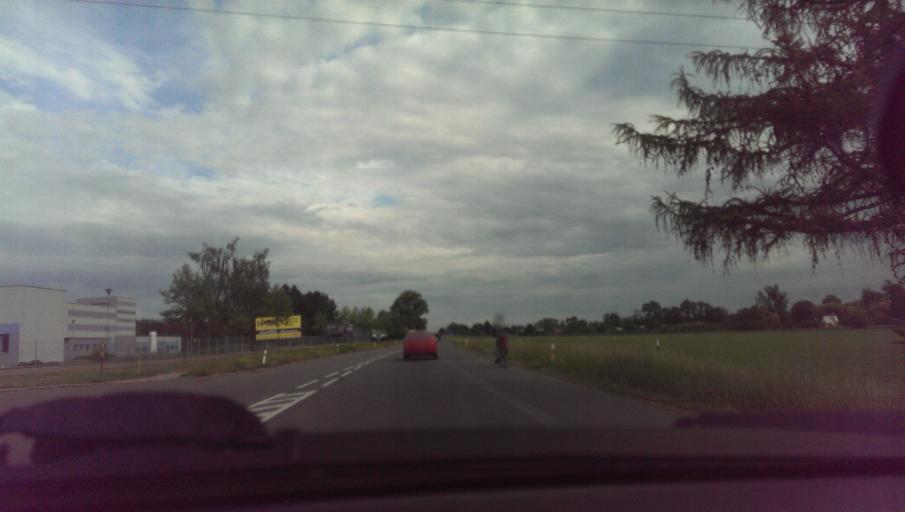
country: CZ
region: Zlin
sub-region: Okres Kromeriz
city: Kromeriz
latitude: 49.3058
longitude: 17.3809
